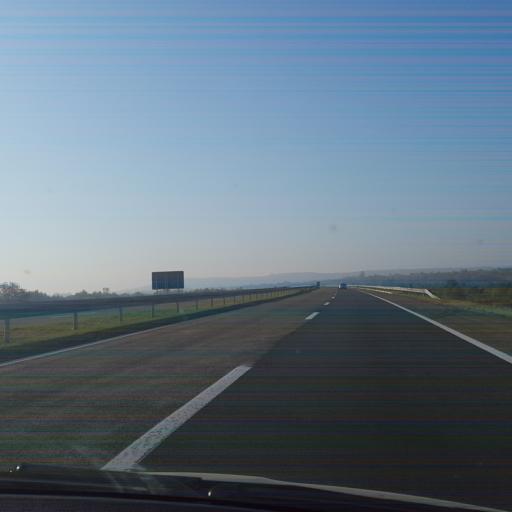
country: RS
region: Central Serbia
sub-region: Nisavski Okrug
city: Merosina
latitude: 43.3062
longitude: 21.7993
